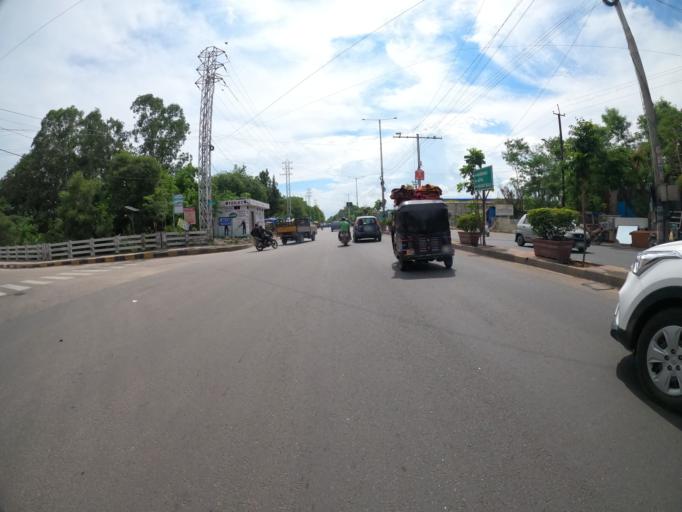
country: IN
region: Telangana
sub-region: Hyderabad
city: Hyderabad
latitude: 17.3730
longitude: 78.4118
